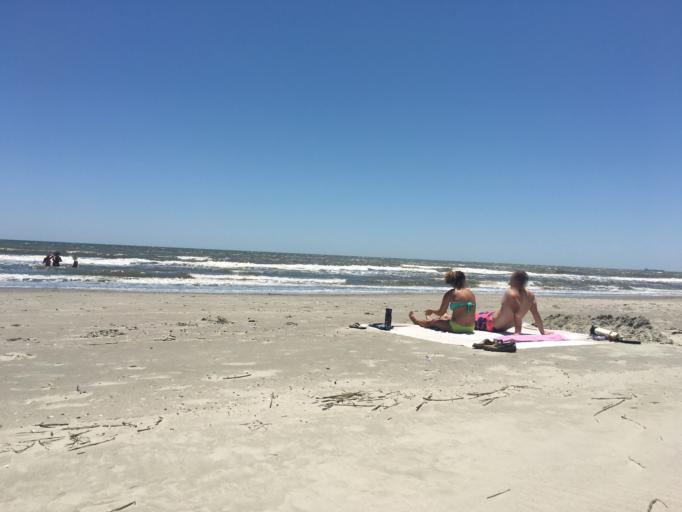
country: US
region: South Carolina
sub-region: Charleston County
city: Isle of Palms
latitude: 32.7918
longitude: -79.7706
